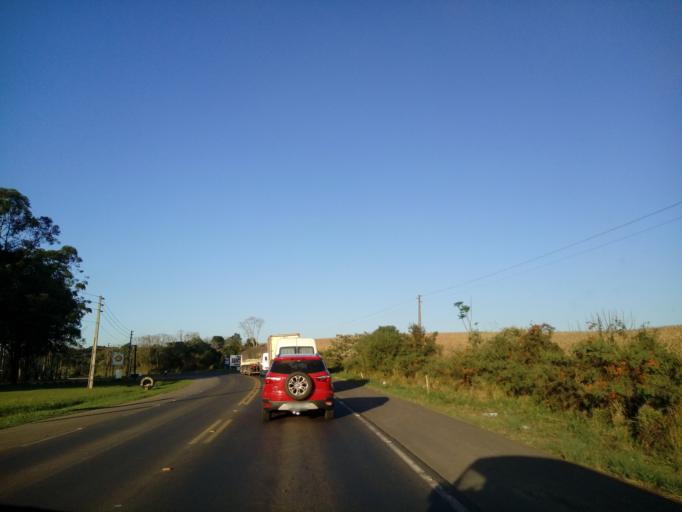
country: BR
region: Santa Catarina
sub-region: Chapeco
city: Chapeco
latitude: -27.2281
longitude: -52.6769
